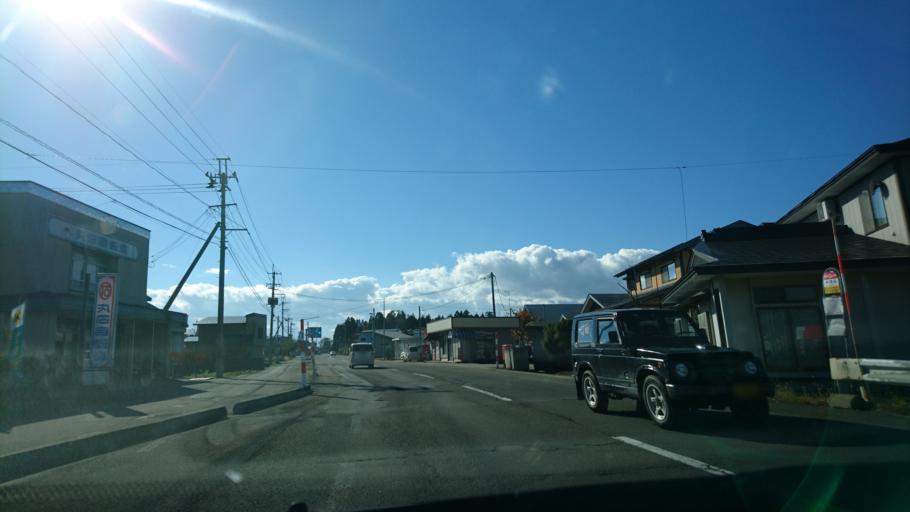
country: JP
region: Akita
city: Yokotemachi
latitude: 39.2760
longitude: 140.5041
